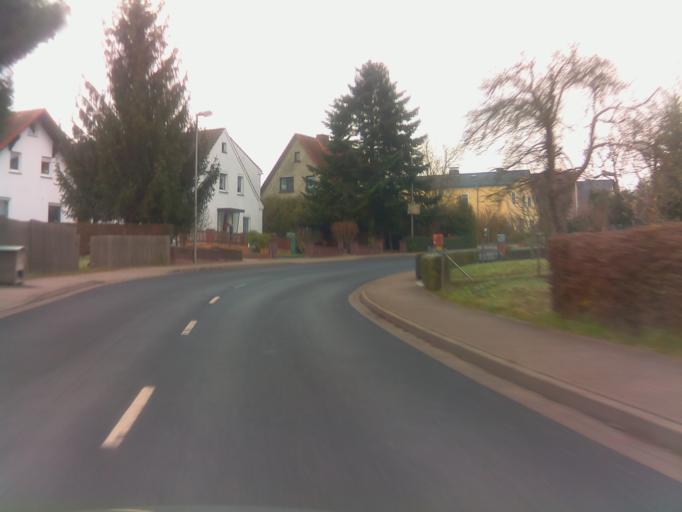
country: DE
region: Thuringia
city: Unterbreizbach
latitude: 50.7926
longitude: 9.9983
